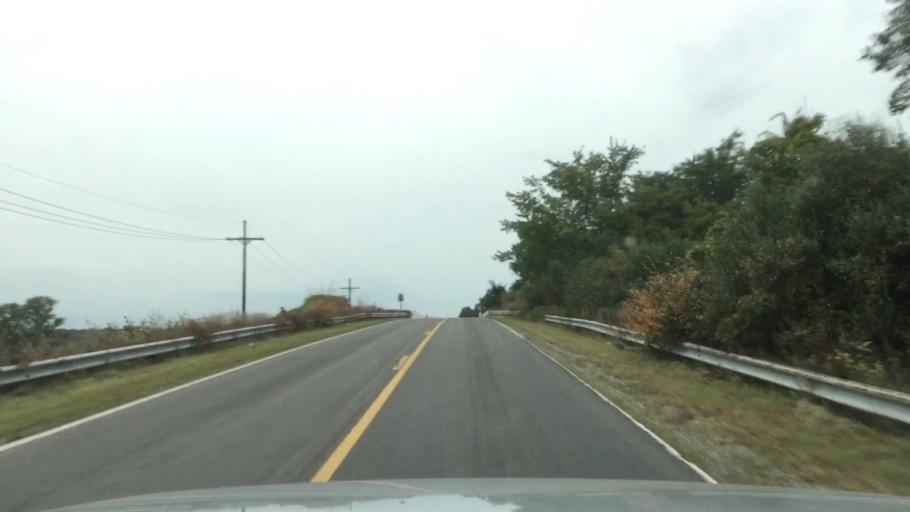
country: US
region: Michigan
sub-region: Washtenaw County
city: Milan
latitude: 42.1132
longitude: -83.6809
